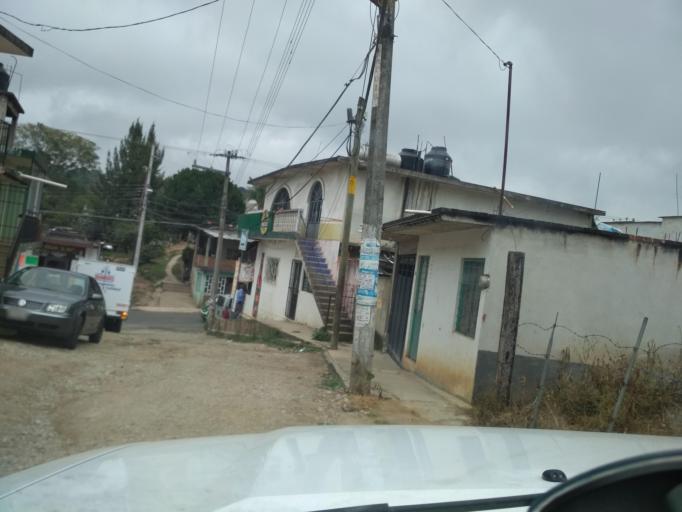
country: MX
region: Veracruz
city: El Castillo
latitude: 19.5471
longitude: -96.8638
